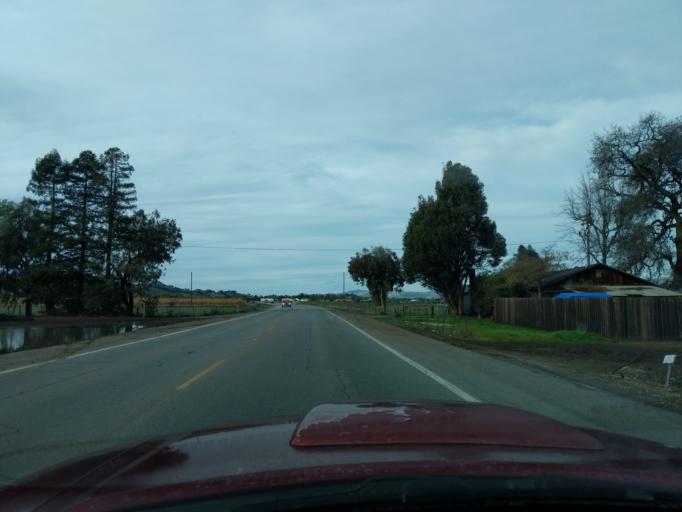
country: US
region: California
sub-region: Santa Clara County
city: San Martin
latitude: 37.0583
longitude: -121.6078
